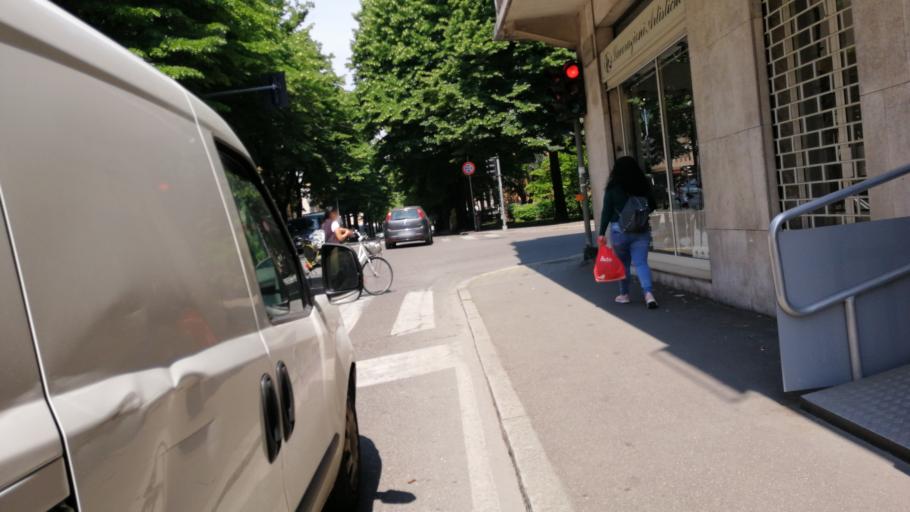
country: IT
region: Emilia-Romagna
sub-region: Provincia di Piacenza
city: Piacenza
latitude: 45.0497
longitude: 9.6871
